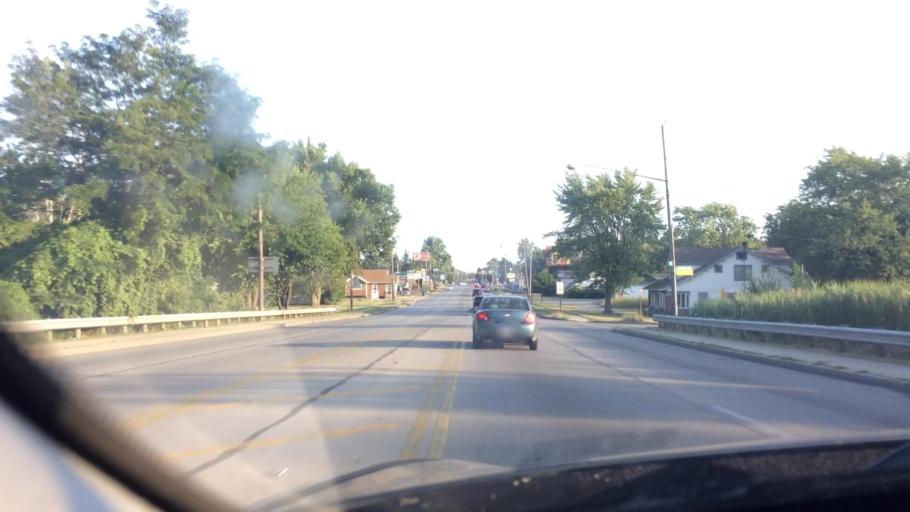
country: US
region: Ohio
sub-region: Lucas County
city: Ottawa Hills
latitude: 41.6288
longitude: -83.6259
